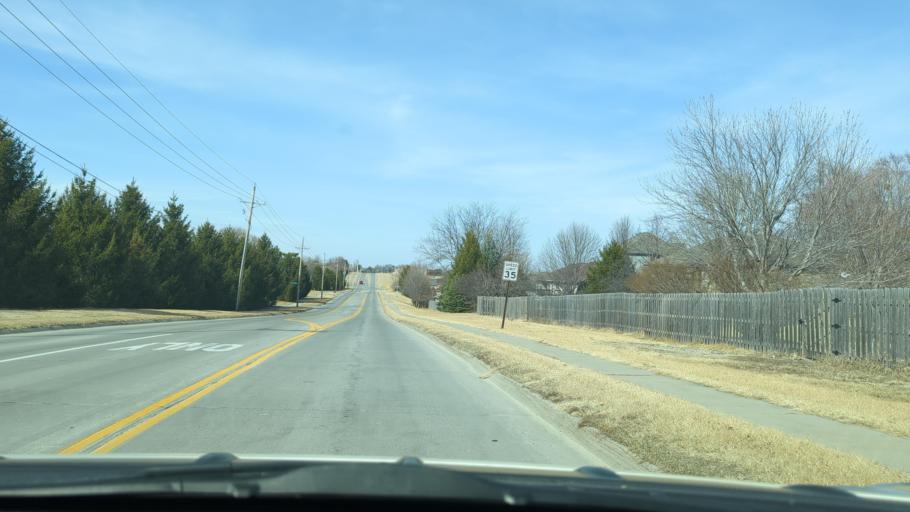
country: US
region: Nebraska
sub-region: Sarpy County
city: Papillion
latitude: 41.1328
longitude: -96.0524
